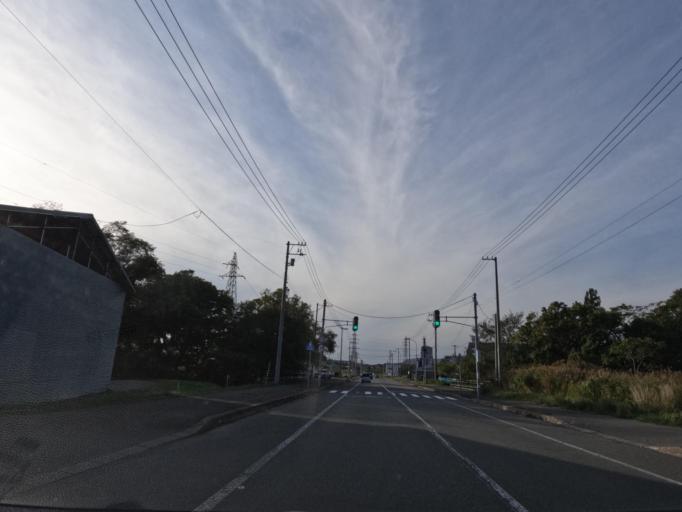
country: JP
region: Hokkaido
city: Date
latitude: 42.4839
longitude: 140.8793
